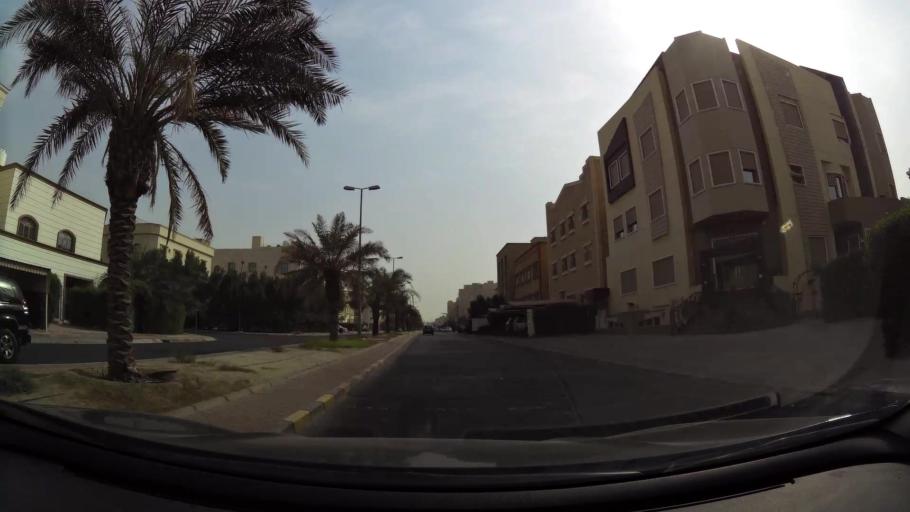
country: KW
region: Al Asimah
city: Ar Rabiyah
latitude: 29.2780
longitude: 47.9383
